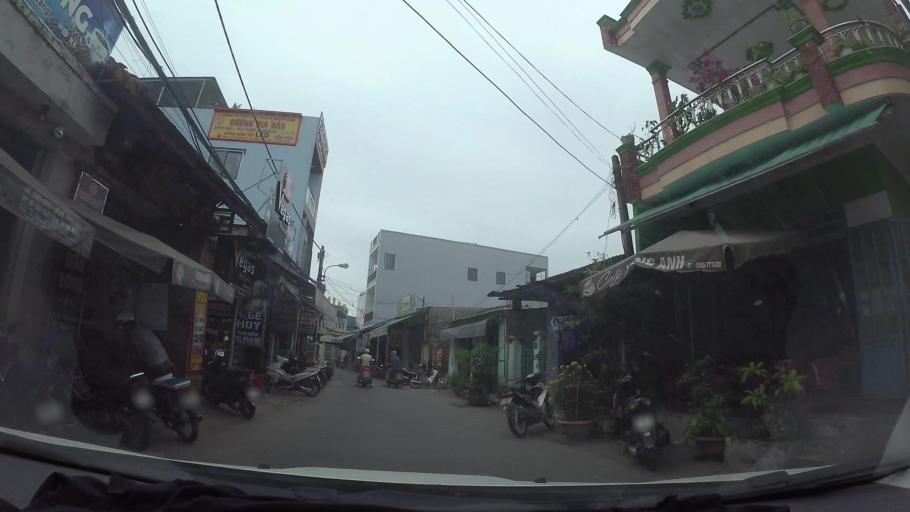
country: VN
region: Da Nang
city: Lien Chieu
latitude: 16.0733
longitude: 108.1456
